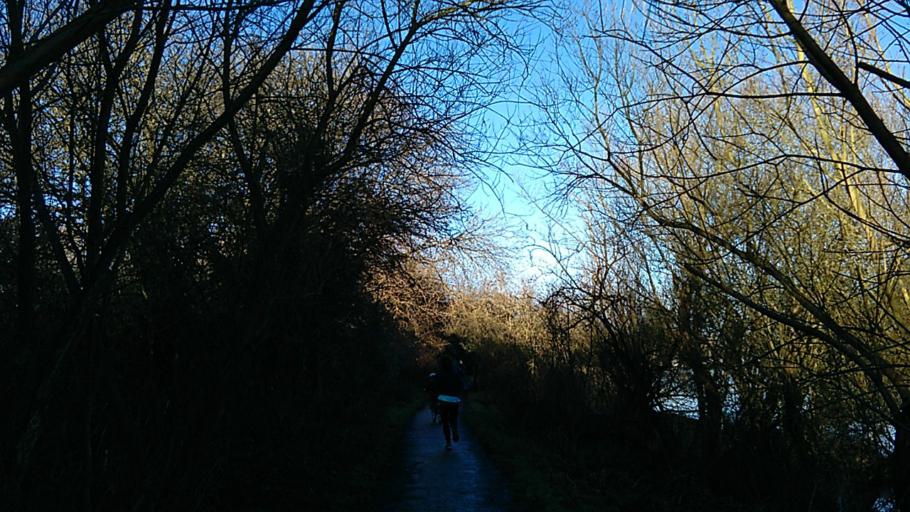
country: GB
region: England
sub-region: Nottinghamshire
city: Gotham
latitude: 52.9085
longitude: -1.2144
